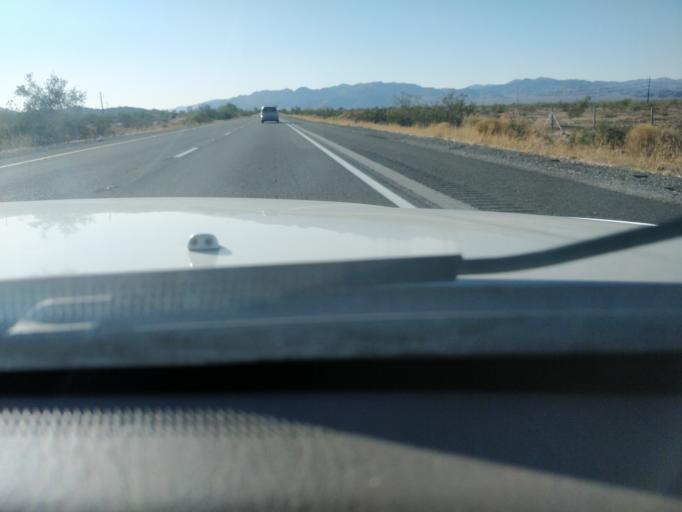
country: US
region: California
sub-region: Imperial County
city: Niland
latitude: 33.7087
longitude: -115.3616
